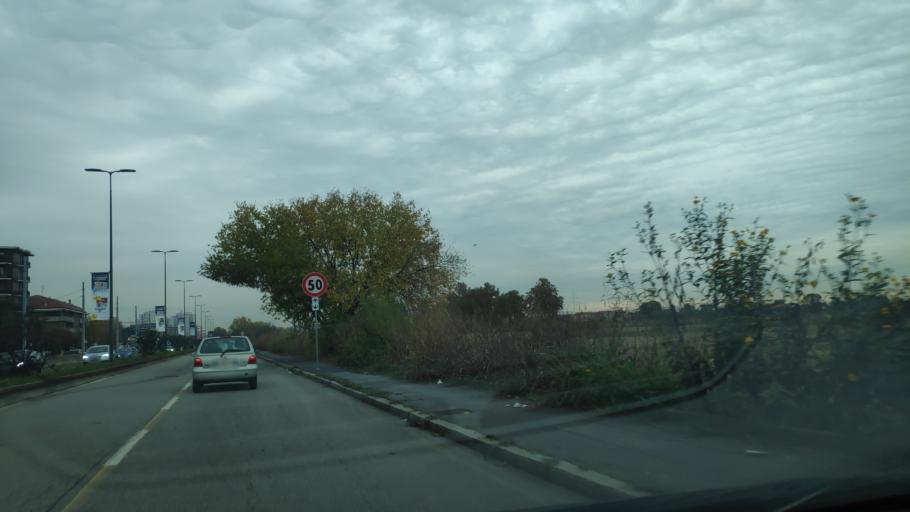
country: IT
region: Lombardy
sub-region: Citta metropolitana di Milano
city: Rozzano
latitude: 45.3954
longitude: 9.1734
